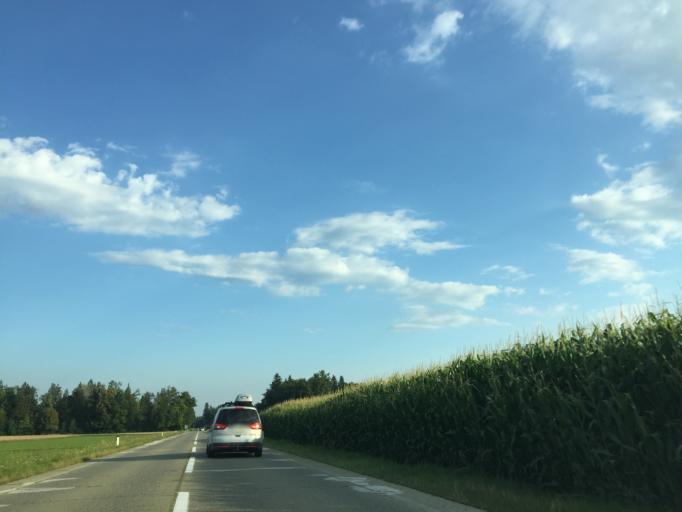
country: SI
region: Sencur
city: Hrastje
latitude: 46.1790
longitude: 14.3823
